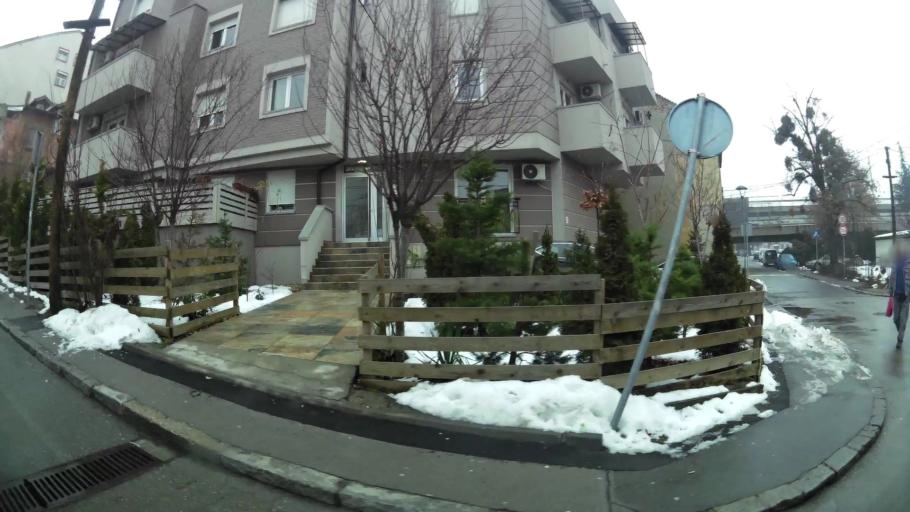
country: RS
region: Central Serbia
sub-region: Belgrade
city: Vracar
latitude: 44.7911
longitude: 20.4644
